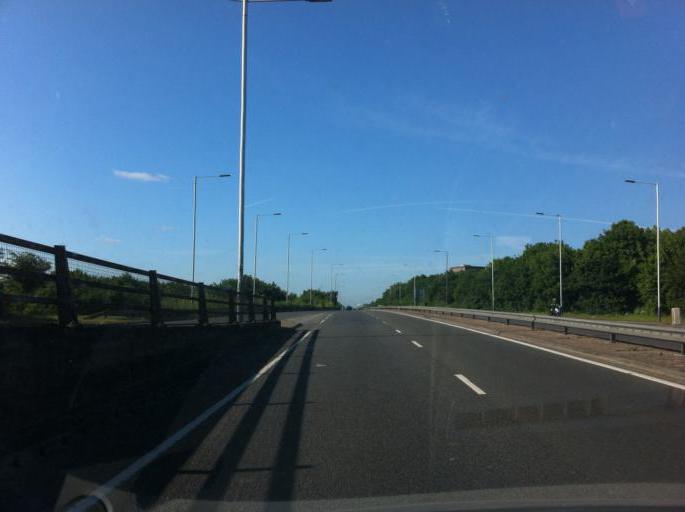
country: GB
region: England
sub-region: Greater London
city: Hayes
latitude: 51.5142
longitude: -0.4023
